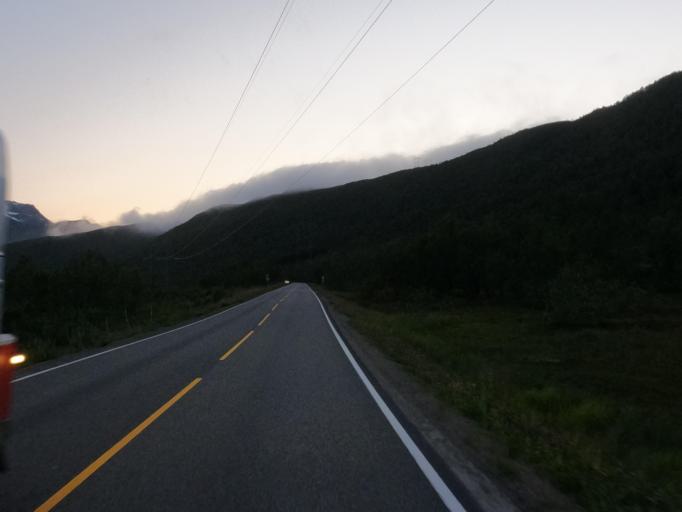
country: NO
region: Nordland
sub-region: Lodingen
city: Lodingen
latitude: 68.5279
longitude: 15.8218
